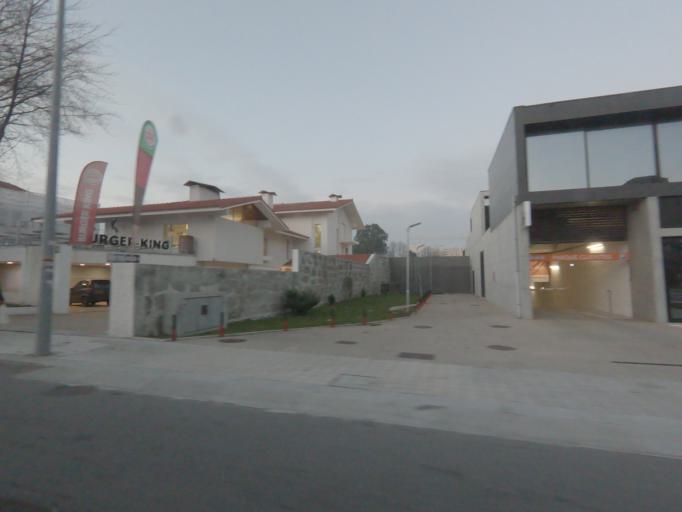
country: PT
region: Porto
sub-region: Matosinhos
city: Senhora da Hora
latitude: 41.1623
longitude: -8.6537
